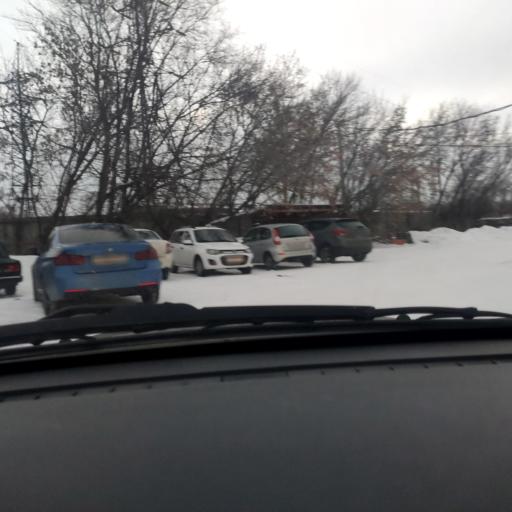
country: RU
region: Samara
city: Tol'yatti
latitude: 53.5296
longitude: 49.4480
